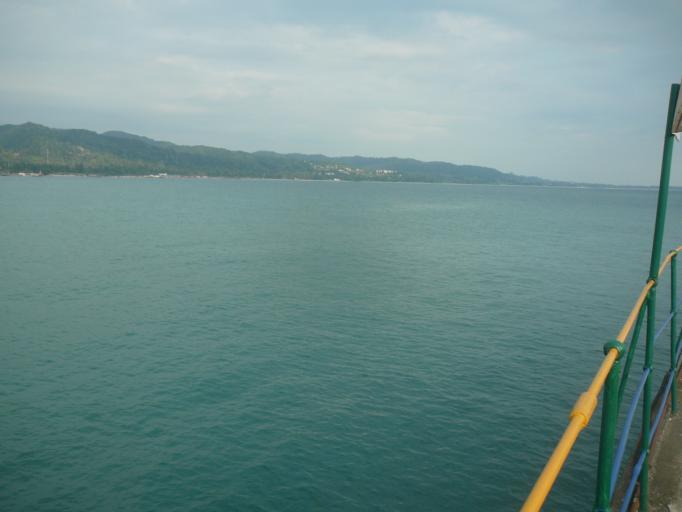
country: GE
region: Abkhazia
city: Sokhumi
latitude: 42.9965
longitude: 41.0232
